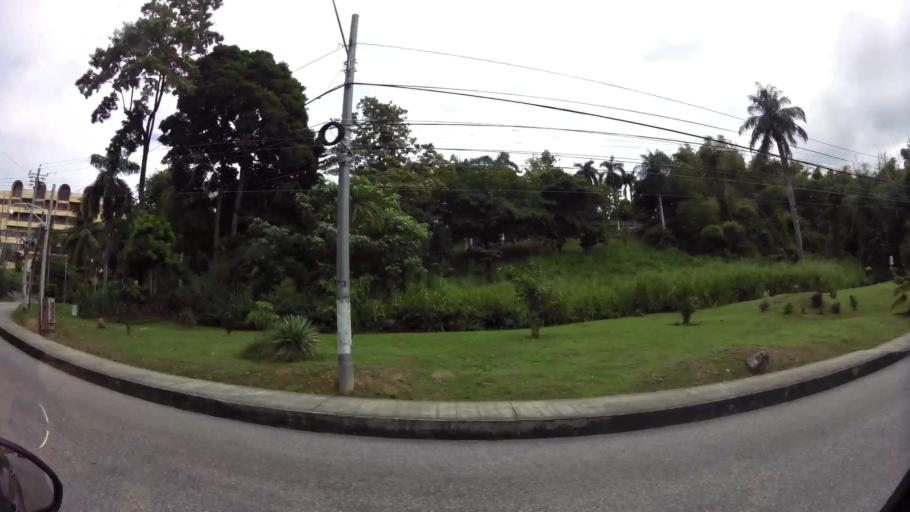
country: TT
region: City of Port of Spain
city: Port-of-Spain
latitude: 10.6810
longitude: -61.5310
